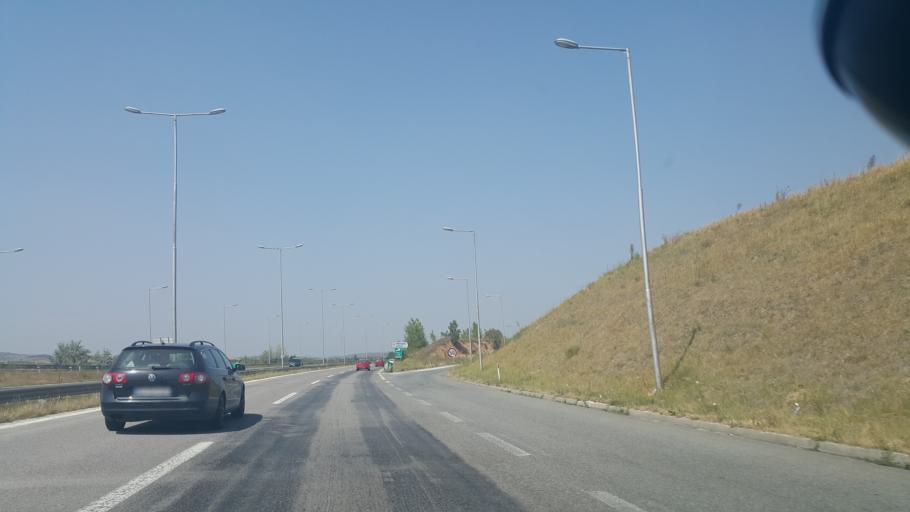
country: MK
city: Miladinovci
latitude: 41.9593
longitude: 21.6323
